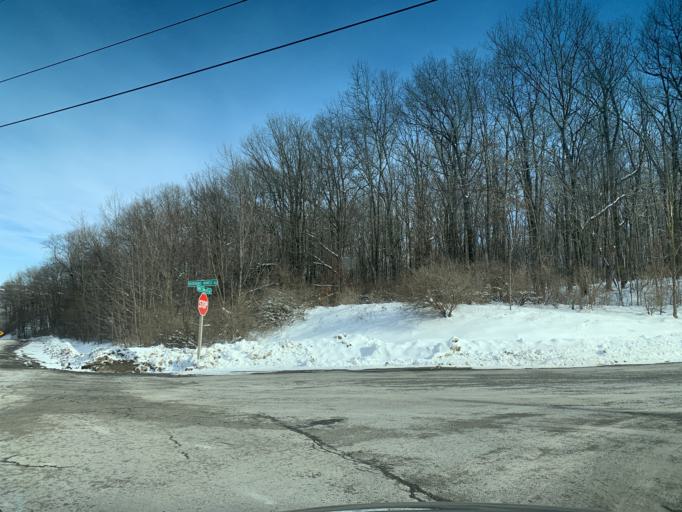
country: US
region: Maryland
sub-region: Allegany County
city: Frostburg
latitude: 39.6199
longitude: -78.9141
